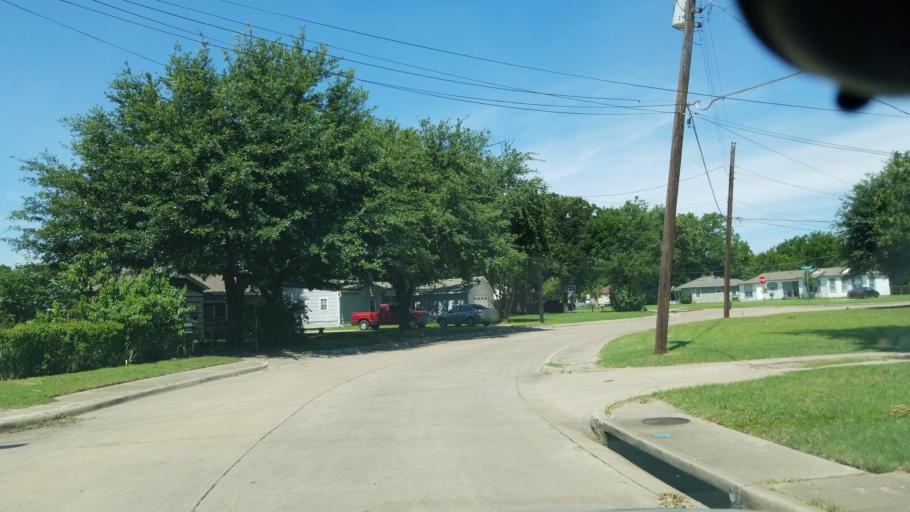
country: US
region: Texas
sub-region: Dallas County
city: Irving
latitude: 32.8196
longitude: -96.9314
